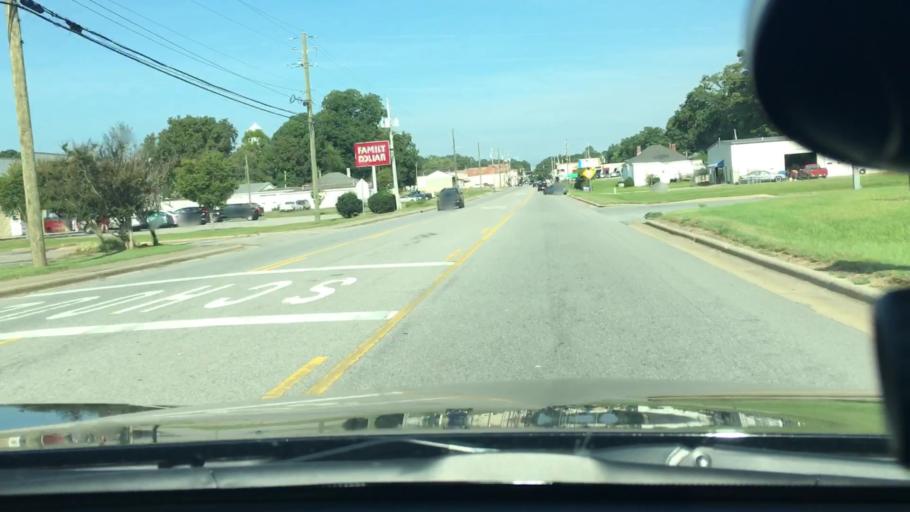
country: US
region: North Carolina
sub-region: Edgecombe County
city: Pinetops
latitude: 35.7895
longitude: -77.6334
